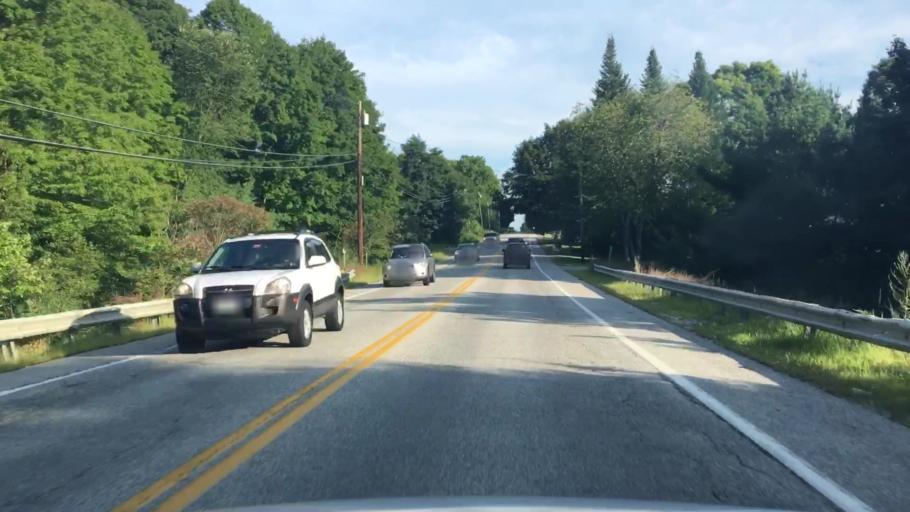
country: US
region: Maine
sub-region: Cumberland County
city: South Windham
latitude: 43.7418
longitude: -70.4219
